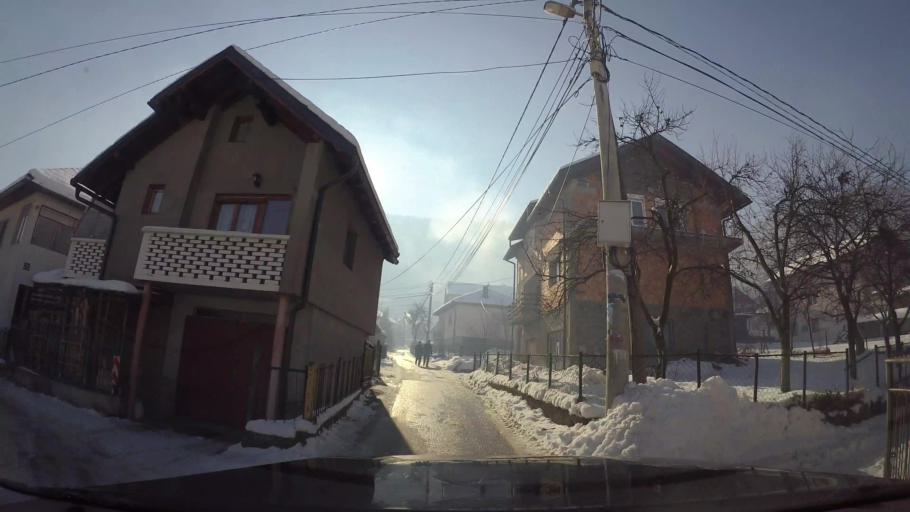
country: BA
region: Federation of Bosnia and Herzegovina
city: Gracanica
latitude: 43.7926
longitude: 18.3164
